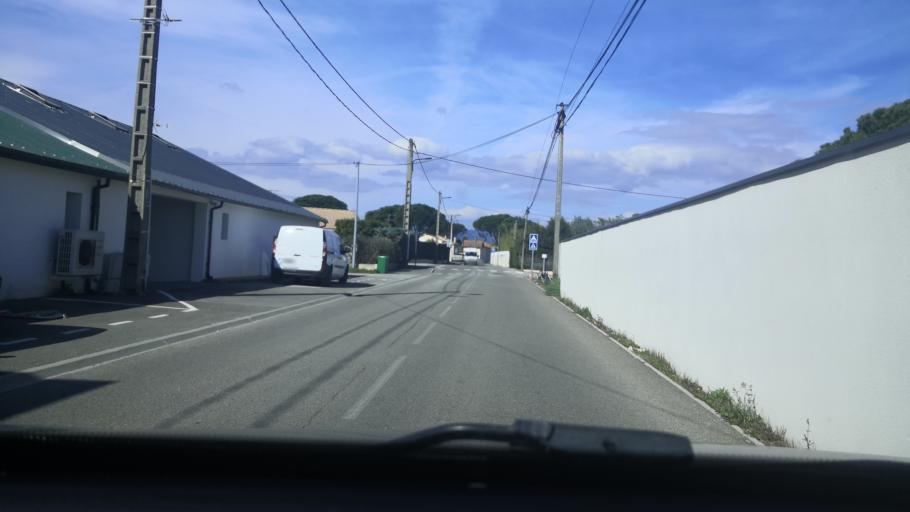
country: FR
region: Rhone-Alpes
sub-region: Departement de la Drome
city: Montelimar
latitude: 44.5439
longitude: 4.7607
